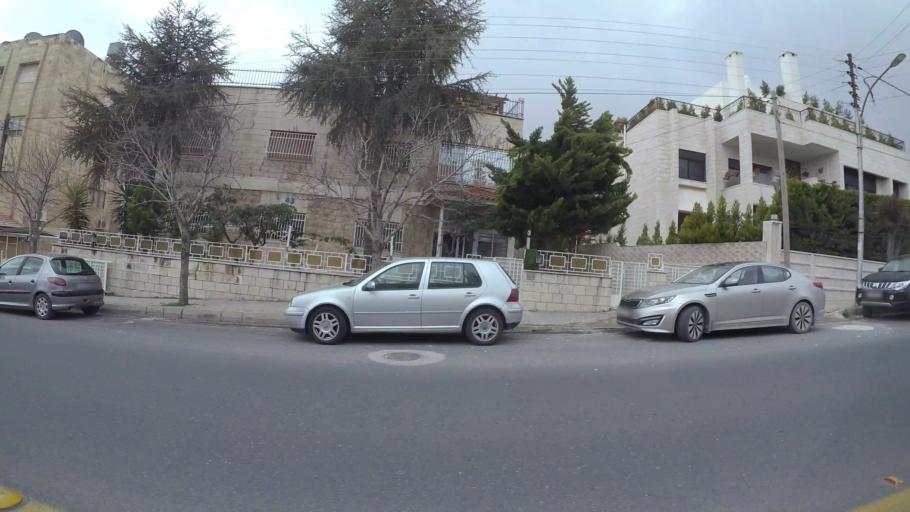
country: JO
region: Amman
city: Wadi as Sir
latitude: 31.9654
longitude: 35.8526
